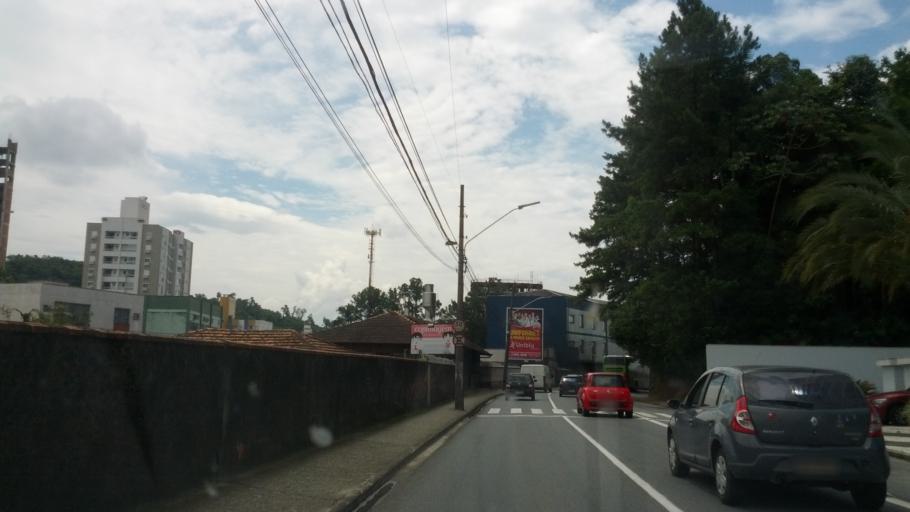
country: BR
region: Santa Catarina
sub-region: Blumenau
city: Blumenau
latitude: -26.9042
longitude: -49.0768
